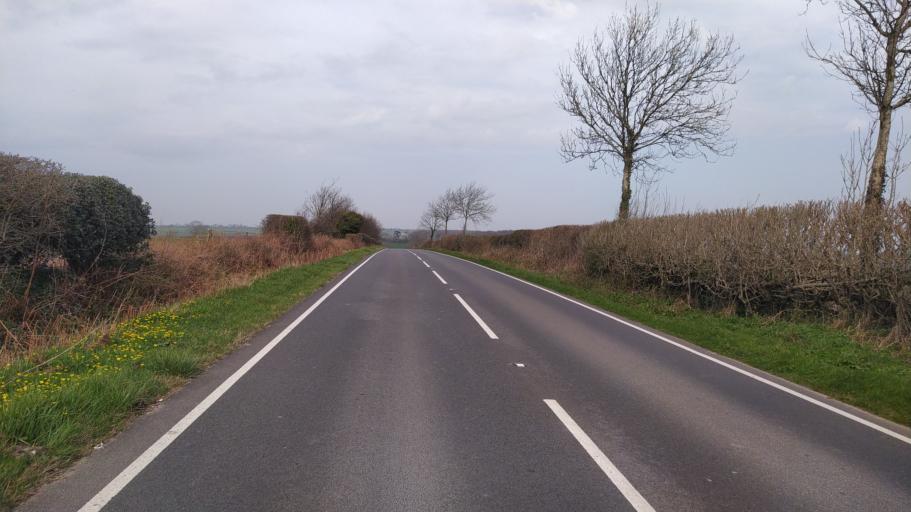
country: GB
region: England
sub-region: Dorset
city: Beaminster
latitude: 50.8111
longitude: -2.6463
